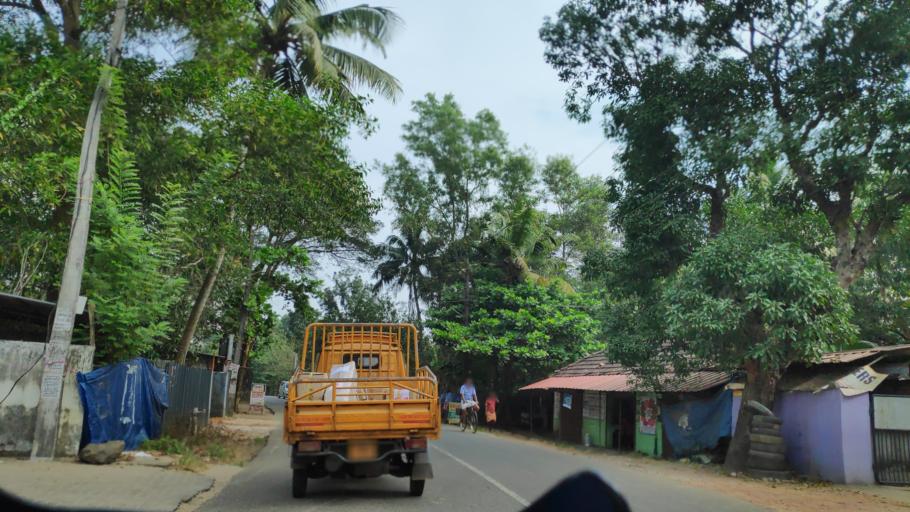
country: IN
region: Kerala
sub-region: Kottayam
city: Vaikam
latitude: 9.7370
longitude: 76.3624
